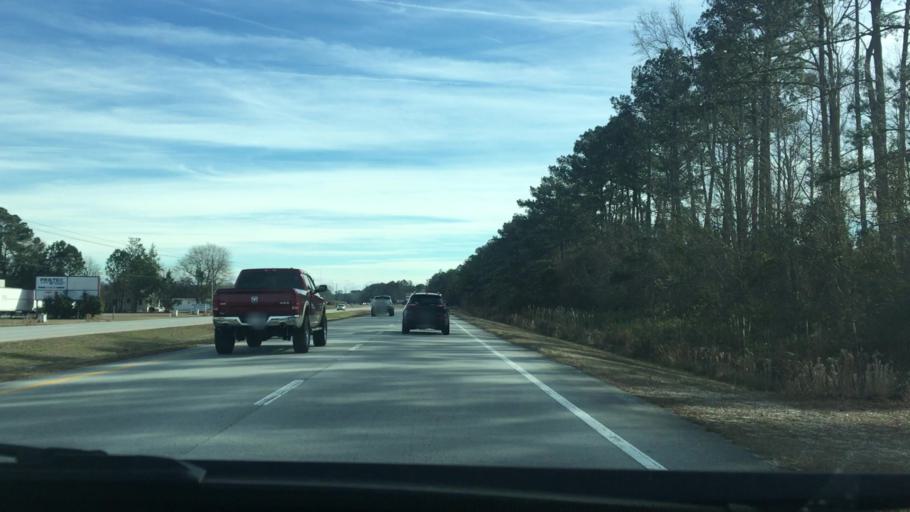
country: US
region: North Carolina
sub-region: Carteret County
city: Newport
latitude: 34.7540
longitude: -76.8448
